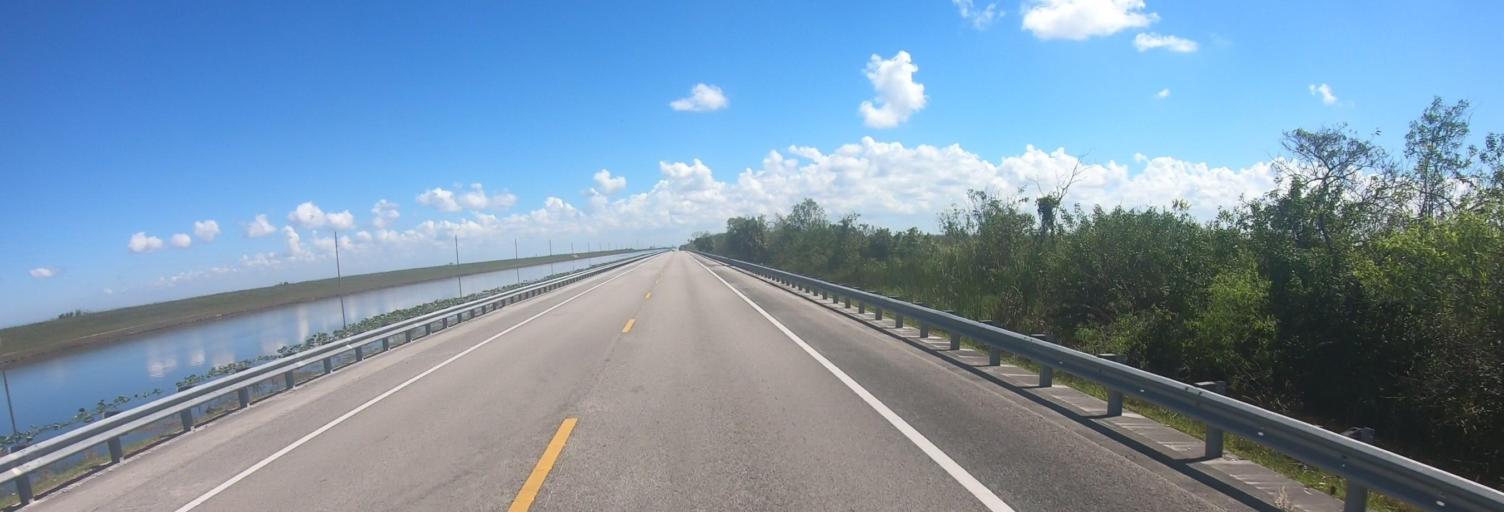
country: US
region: Florida
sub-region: Miami-Dade County
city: Kendall West
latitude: 25.7605
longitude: -80.5758
